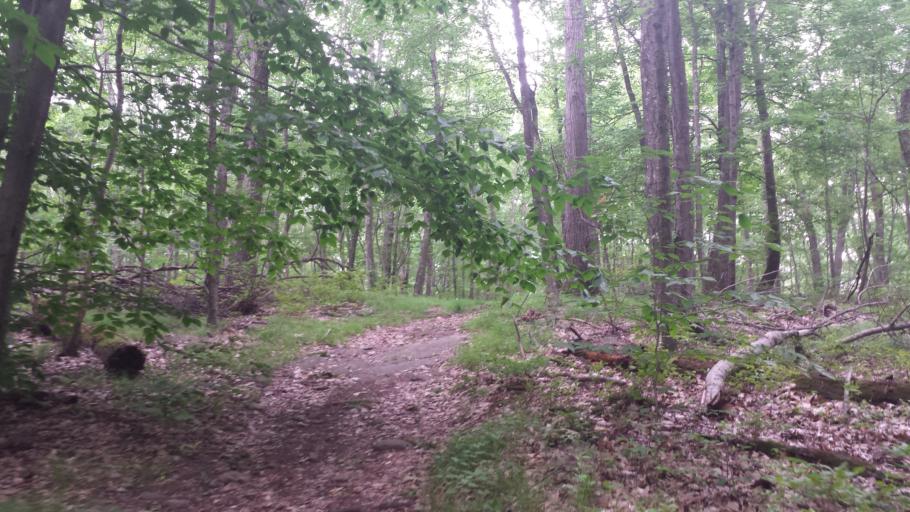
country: US
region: New York
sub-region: Westchester County
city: Pound Ridge
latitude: 41.2685
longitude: -73.5810
